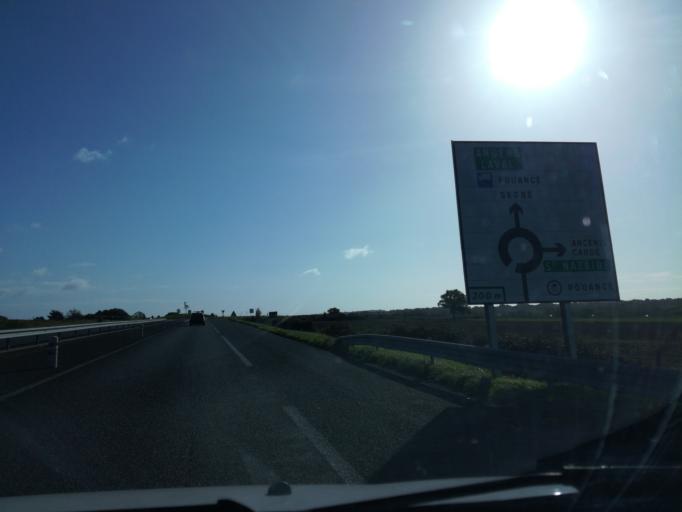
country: FR
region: Pays de la Loire
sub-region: Departement de Maine-et-Loire
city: Pouance
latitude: 47.7616
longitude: -1.2071
